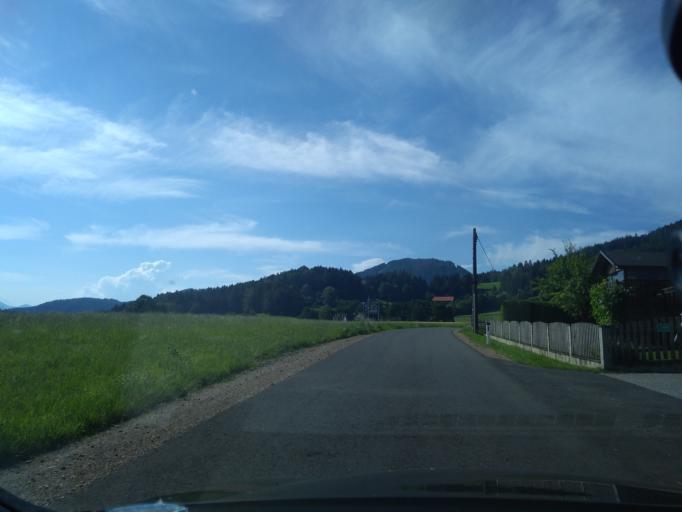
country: AT
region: Styria
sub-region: Politischer Bezirk Graz-Umgebung
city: Semriach
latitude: 47.2386
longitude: 15.3912
